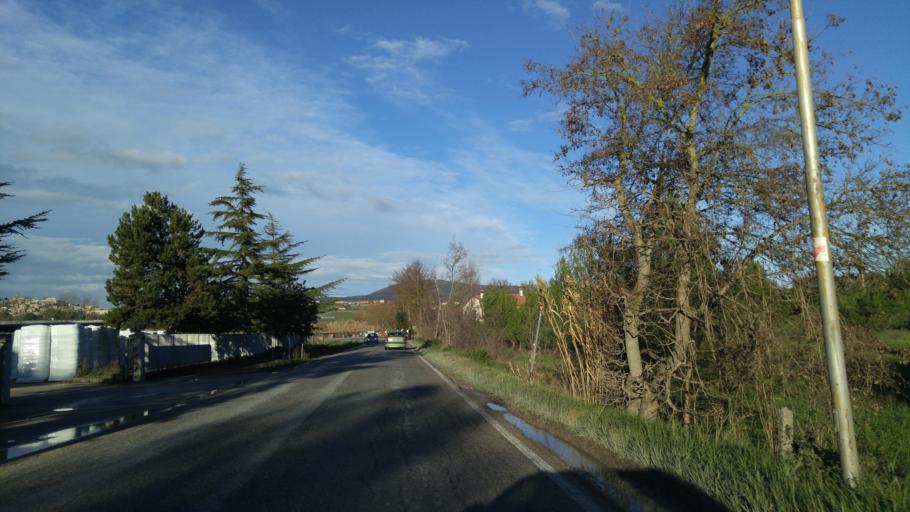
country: IT
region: The Marches
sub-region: Provincia di Ancona
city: Camerano
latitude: 43.5014
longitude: 13.5448
